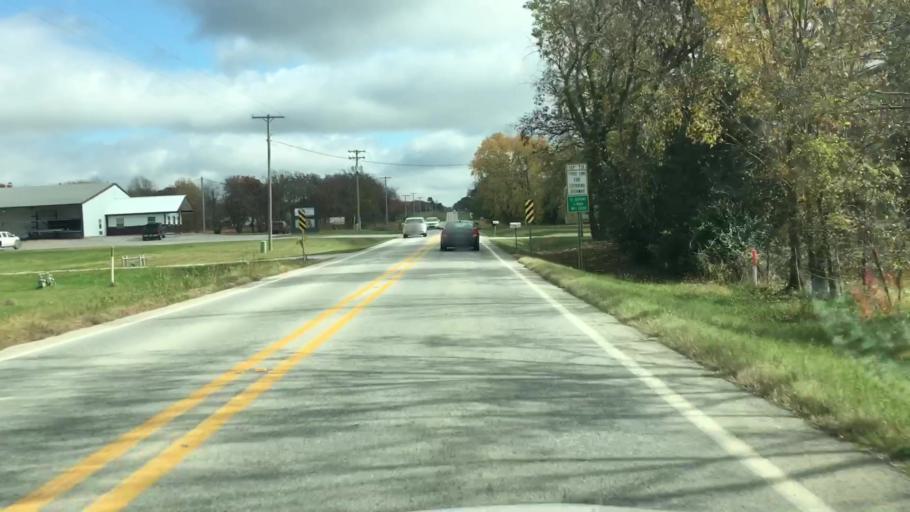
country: US
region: Arkansas
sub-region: Benton County
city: Gentry
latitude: 36.2635
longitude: -94.4632
